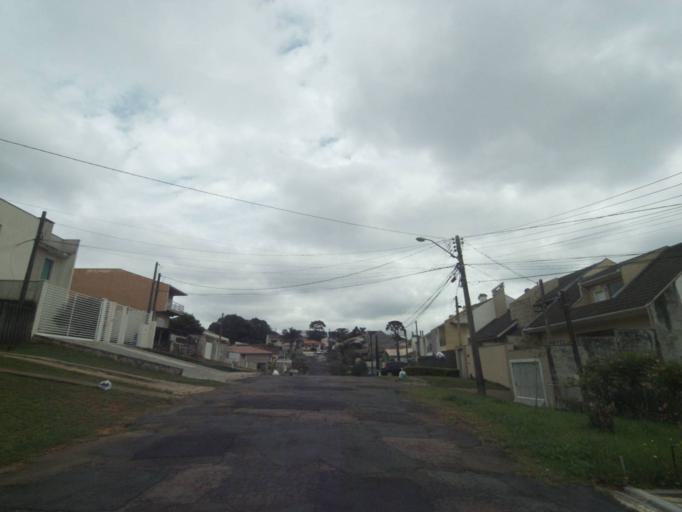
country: BR
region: Parana
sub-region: Curitiba
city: Curitiba
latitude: -25.3878
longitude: -49.2760
